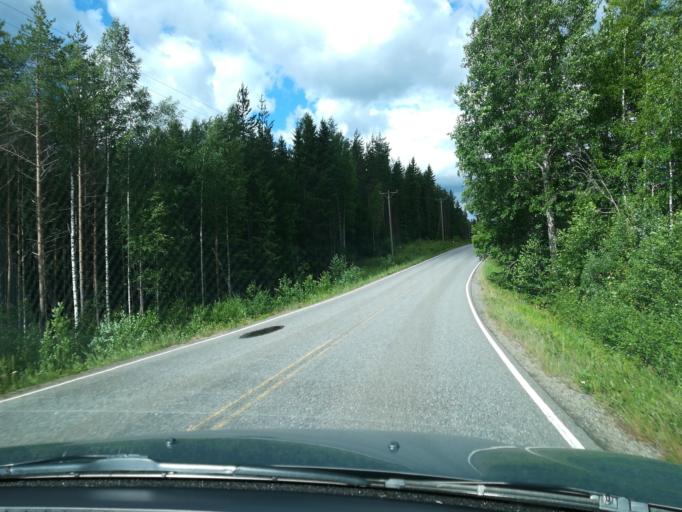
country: FI
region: Southern Savonia
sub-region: Mikkeli
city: Ristiina
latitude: 61.3533
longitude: 27.1182
